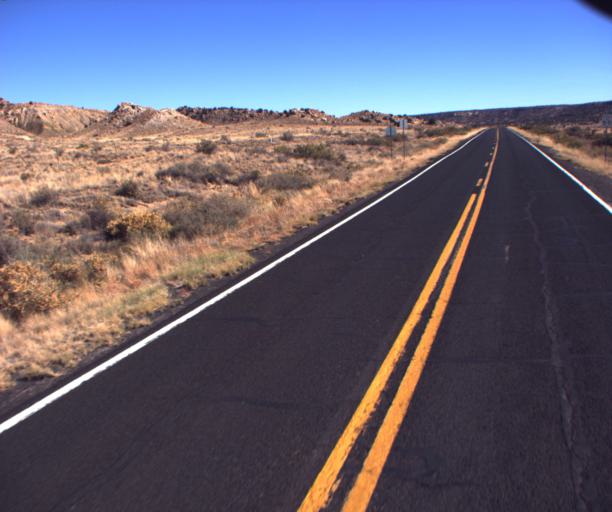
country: US
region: Arizona
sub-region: Navajo County
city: First Mesa
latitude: 35.8306
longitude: -110.2898
